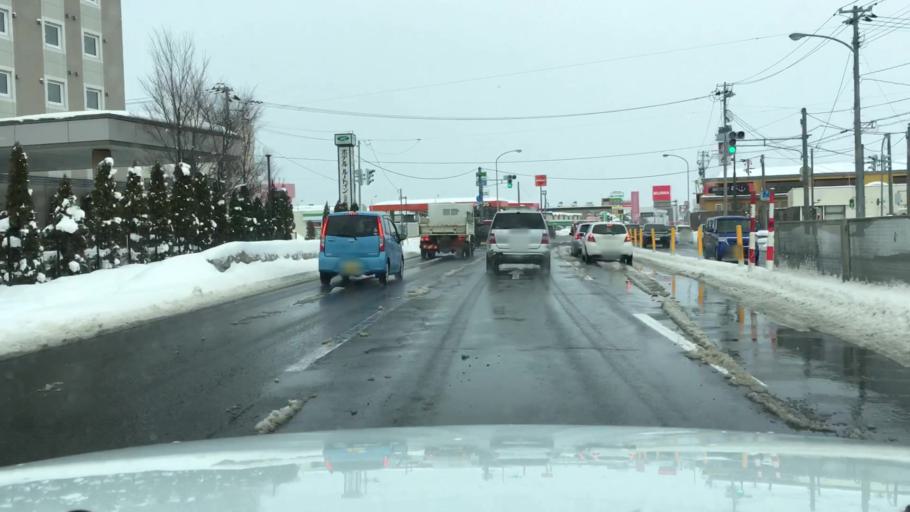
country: JP
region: Aomori
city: Hirosaki
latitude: 40.6031
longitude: 140.4994
